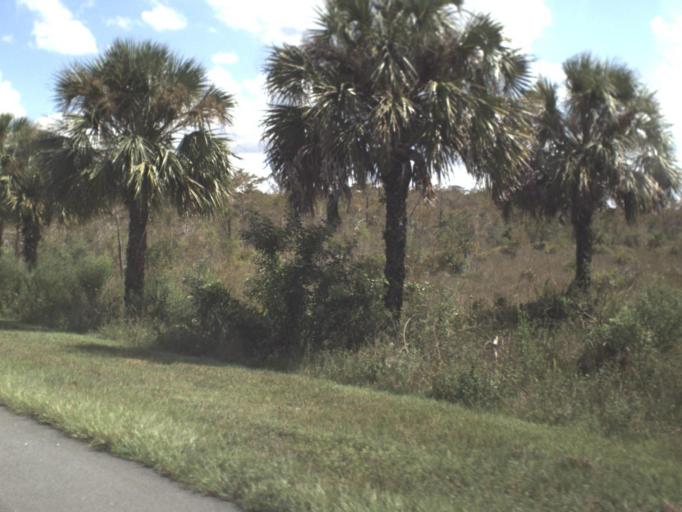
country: US
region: Florida
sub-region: Collier County
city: Marco
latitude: 25.8722
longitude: -81.1841
